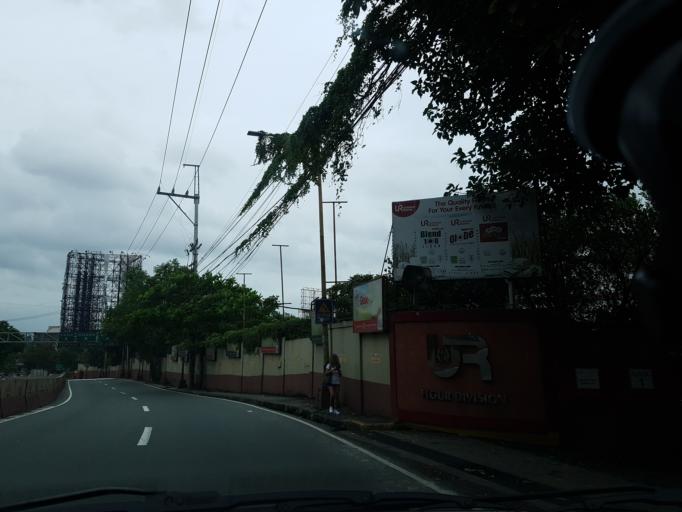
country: PH
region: Calabarzon
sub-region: Province of Rizal
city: Pateros
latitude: 14.5629
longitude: 121.0666
